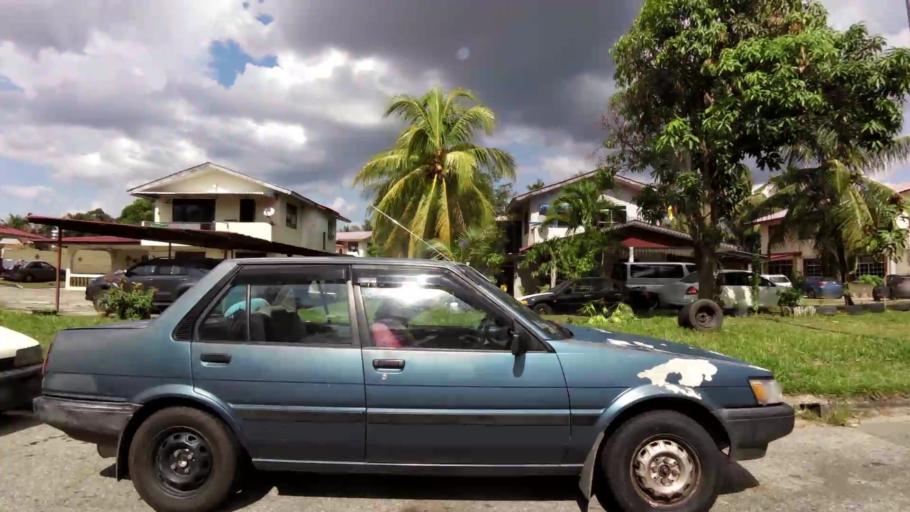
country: BN
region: Brunei and Muara
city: Bandar Seri Begawan
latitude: 4.9581
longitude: 114.9591
